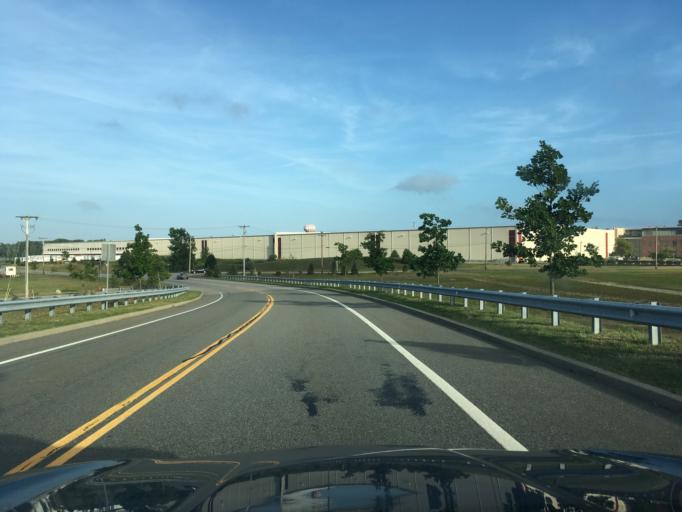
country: US
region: Rhode Island
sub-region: Kent County
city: East Greenwich
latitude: 41.6071
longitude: -71.4376
